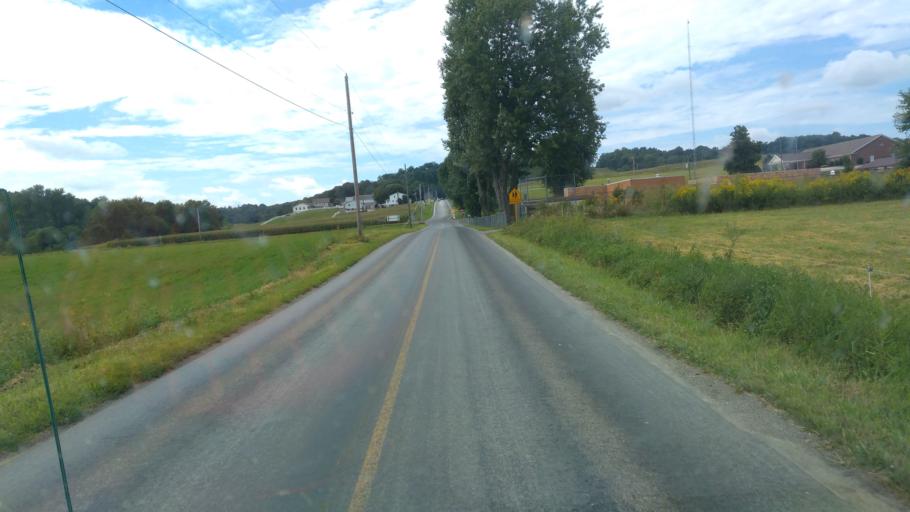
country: US
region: Ohio
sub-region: Holmes County
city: Millersburg
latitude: 40.5355
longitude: -81.8097
